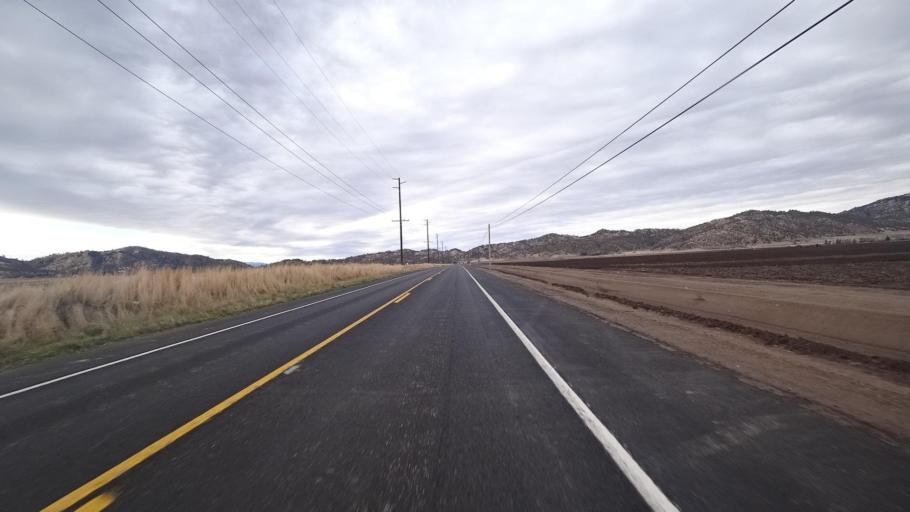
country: US
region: California
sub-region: Kern County
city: Stallion Springs
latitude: 35.0946
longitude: -118.6165
